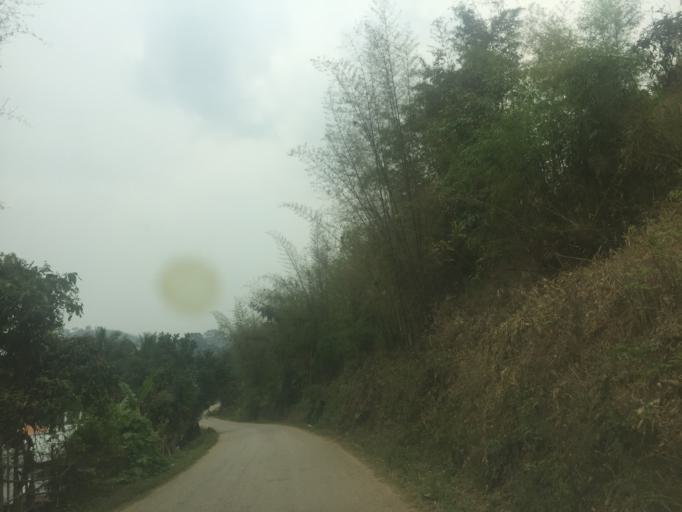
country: LA
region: Vientiane
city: Muang Sanakham
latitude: 18.4011
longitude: 101.5153
